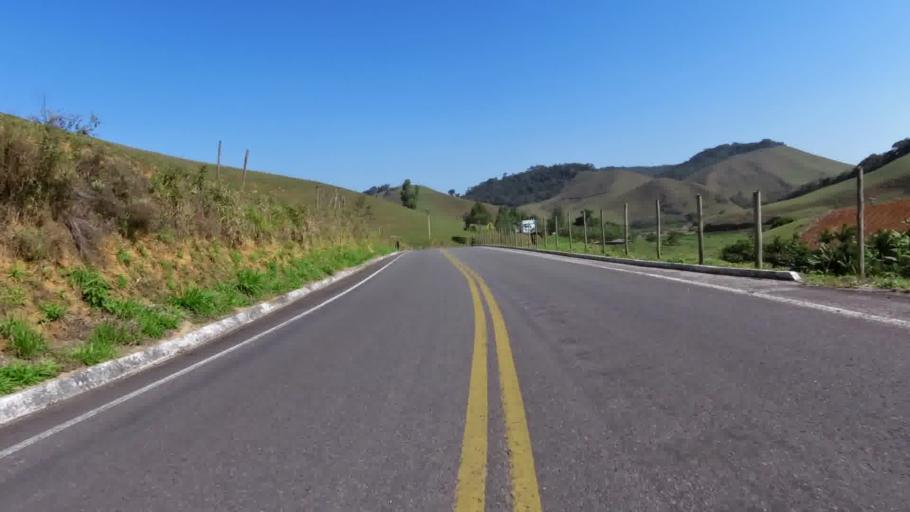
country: BR
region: Espirito Santo
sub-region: Alfredo Chaves
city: Alfredo Chaves
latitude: -20.5657
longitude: -40.8062
